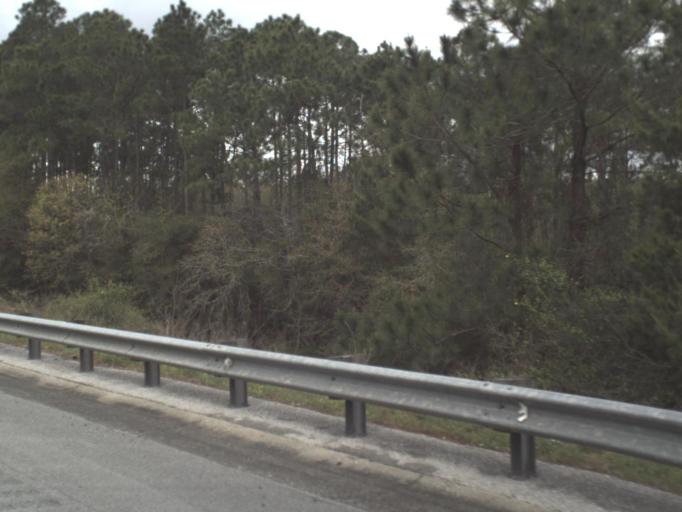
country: US
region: Florida
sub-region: Okaloosa County
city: Crestview
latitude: 30.7223
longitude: -86.5955
